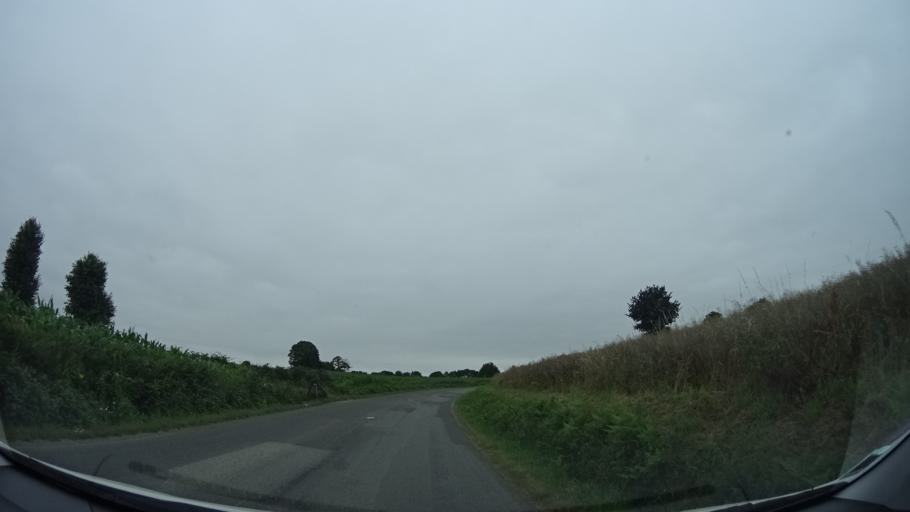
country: FR
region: Brittany
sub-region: Departement d'Ille-et-Vilaine
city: Hede-Bazouges
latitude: 48.2949
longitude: -1.7681
